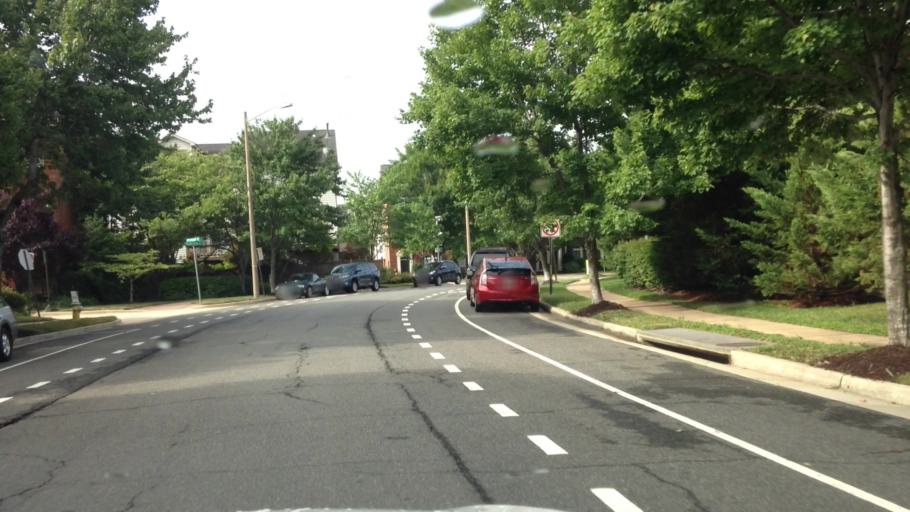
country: US
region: Virginia
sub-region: City of Alexandria
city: Alexandria
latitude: 38.8253
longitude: -77.0462
